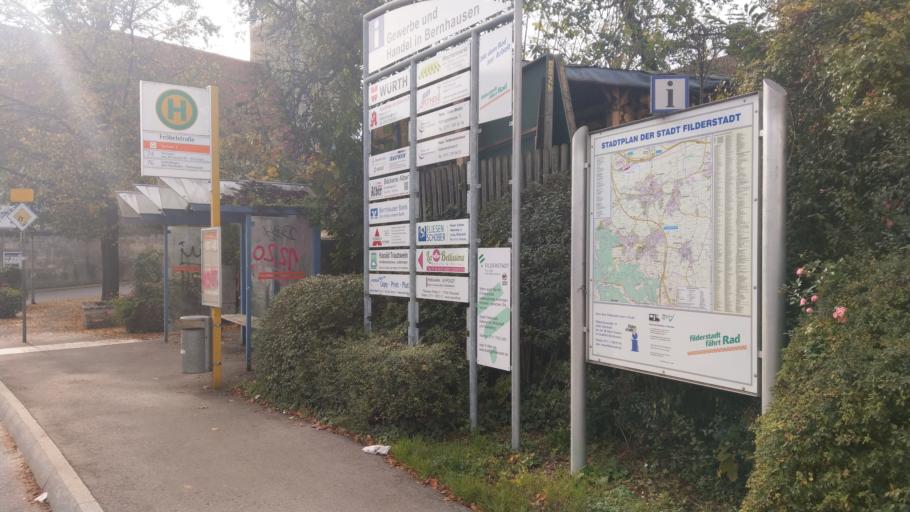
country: DE
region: Baden-Wuerttemberg
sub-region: Regierungsbezirk Stuttgart
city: Filderstadt
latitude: 48.6808
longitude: 9.2187
